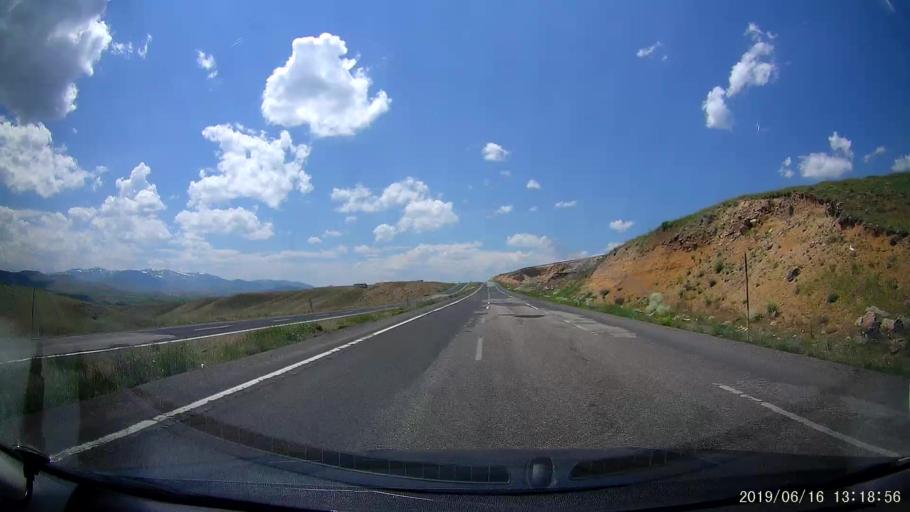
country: TR
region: Agri
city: Taslicay
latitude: 39.6319
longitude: 43.4208
